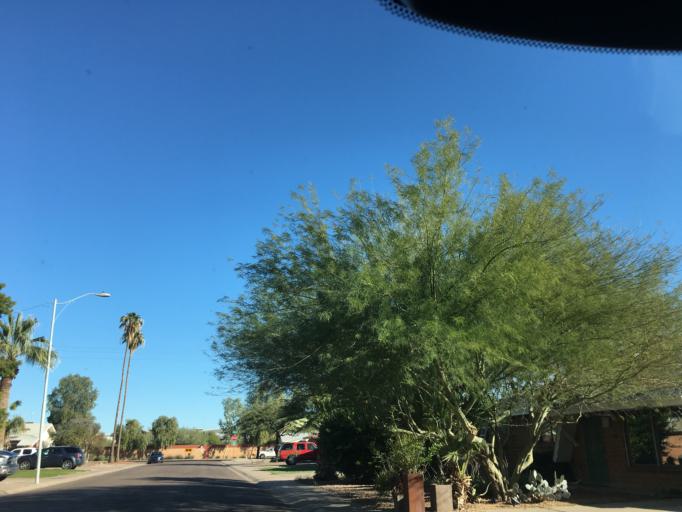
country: US
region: Arizona
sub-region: Maricopa County
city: Scottsdale
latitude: 33.5079
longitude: -111.8929
